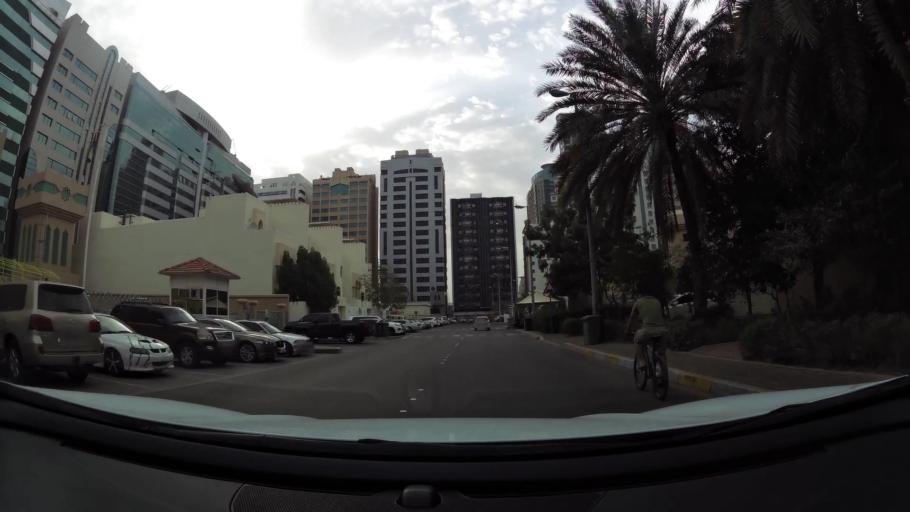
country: AE
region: Abu Dhabi
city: Abu Dhabi
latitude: 24.4743
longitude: 54.3727
